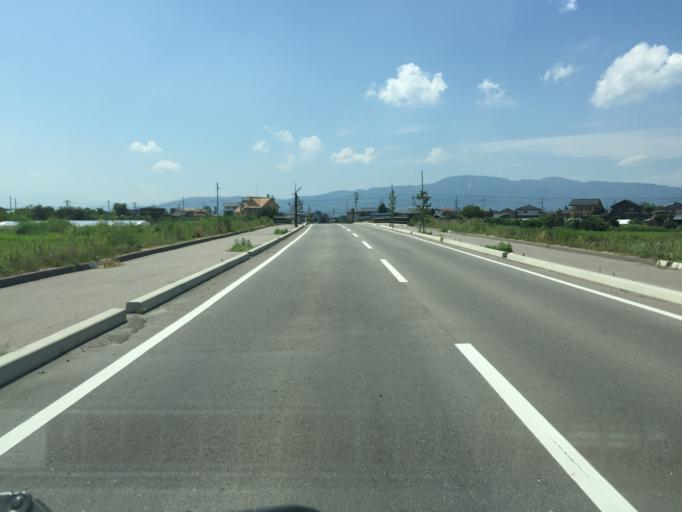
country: JP
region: Fukushima
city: Yanagawamachi-saiwaicho
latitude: 37.8477
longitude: 140.5963
